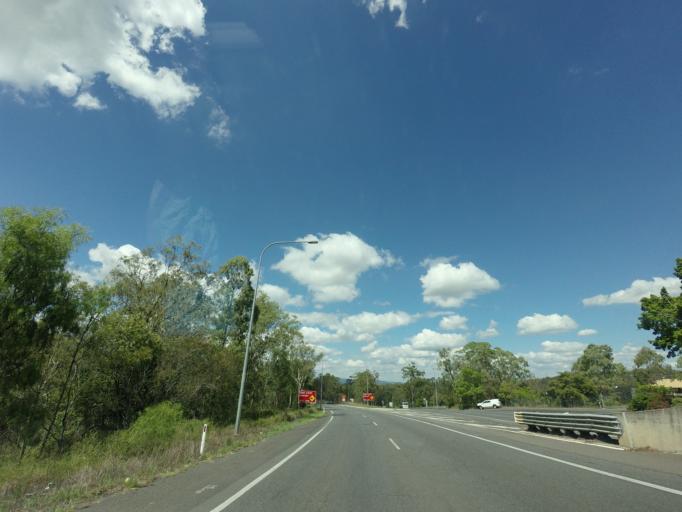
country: AU
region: Queensland
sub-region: Toowoomba
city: East Toowoomba
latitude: -27.5684
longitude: 151.9945
